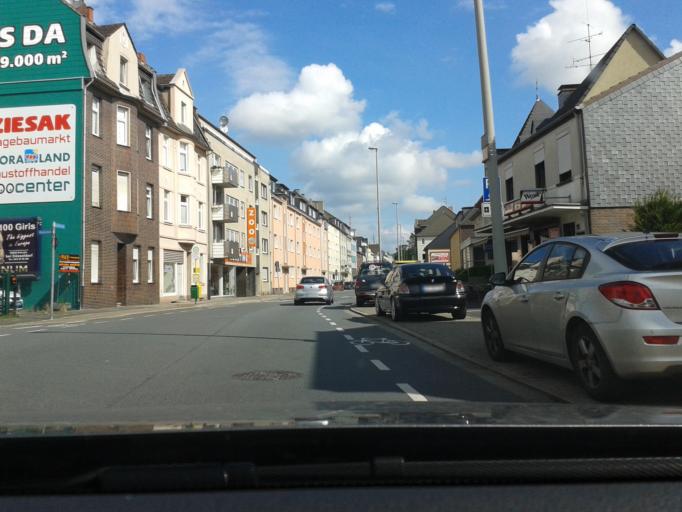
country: DE
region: North Rhine-Westphalia
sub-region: Regierungsbezirk Dusseldorf
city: Oberhausen
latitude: 51.4596
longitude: 6.8513
